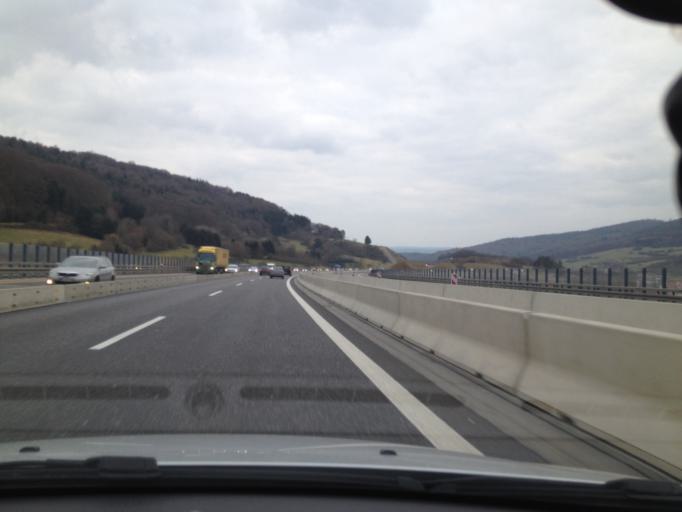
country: DE
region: Bavaria
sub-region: Regierungsbezirk Unterfranken
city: Waldaschaff
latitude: 49.9632
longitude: 9.3061
